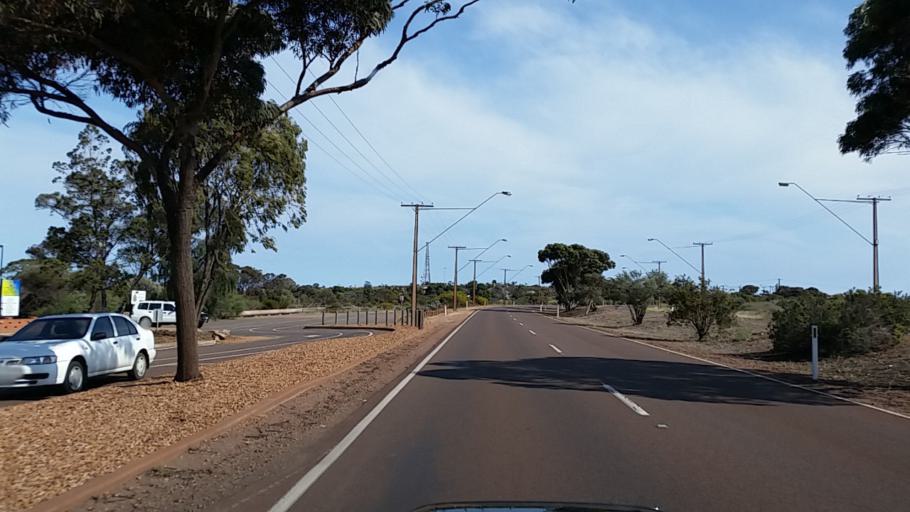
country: AU
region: South Australia
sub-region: Whyalla
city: Whyalla
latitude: -33.0193
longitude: 137.5747
